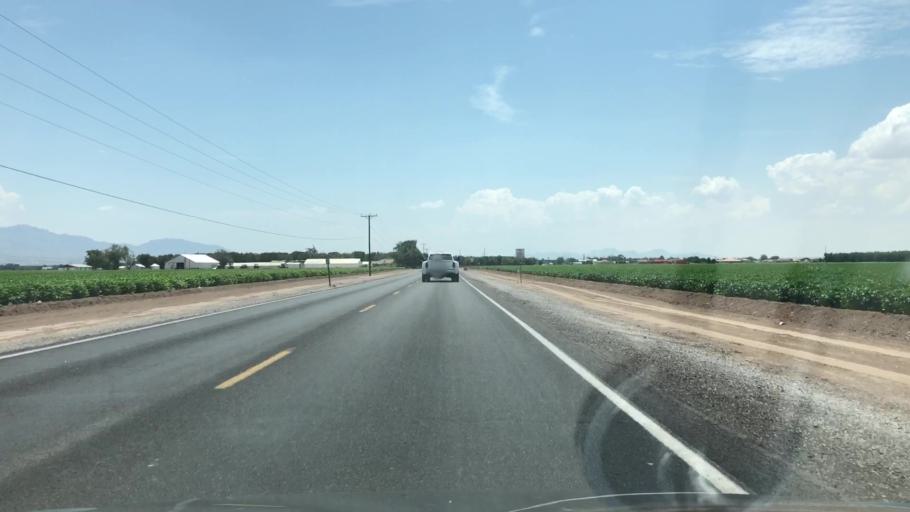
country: US
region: New Mexico
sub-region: Dona Ana County
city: La Union
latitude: 31.9672
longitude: -106.6500
